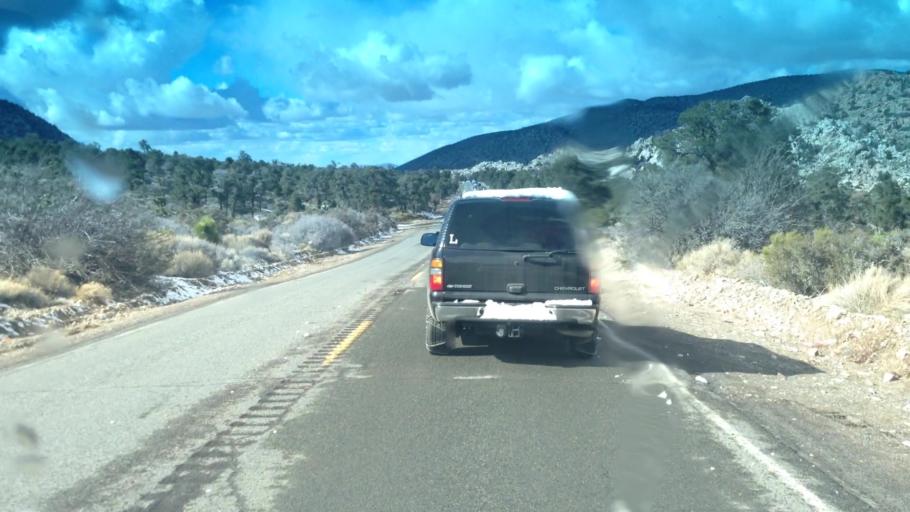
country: US
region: California
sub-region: San Bernardino County
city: Big Bear City
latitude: 34.3088
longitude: -116.8066
